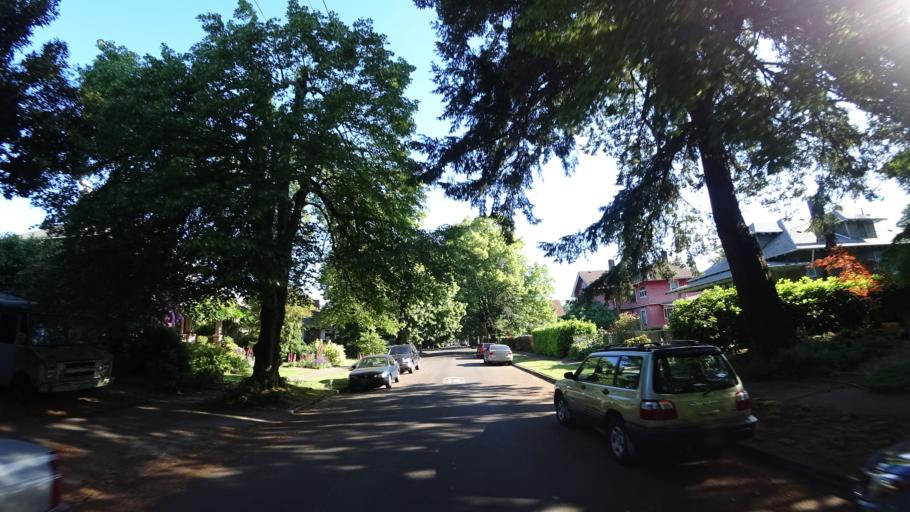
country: US
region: Oregon
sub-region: Multnomah County
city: Portland
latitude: 45.5658
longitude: -122.6669
